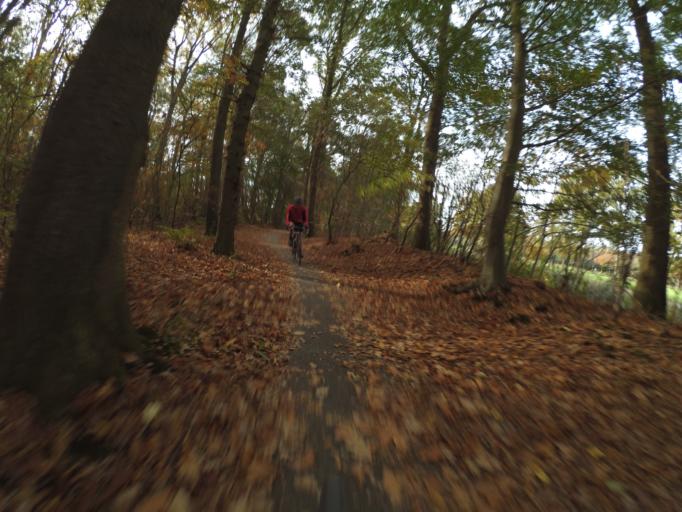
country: NL
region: Overijssel
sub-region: Gemeente Deventer
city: Schalkhaar
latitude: 52.3051
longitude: 6.2547
